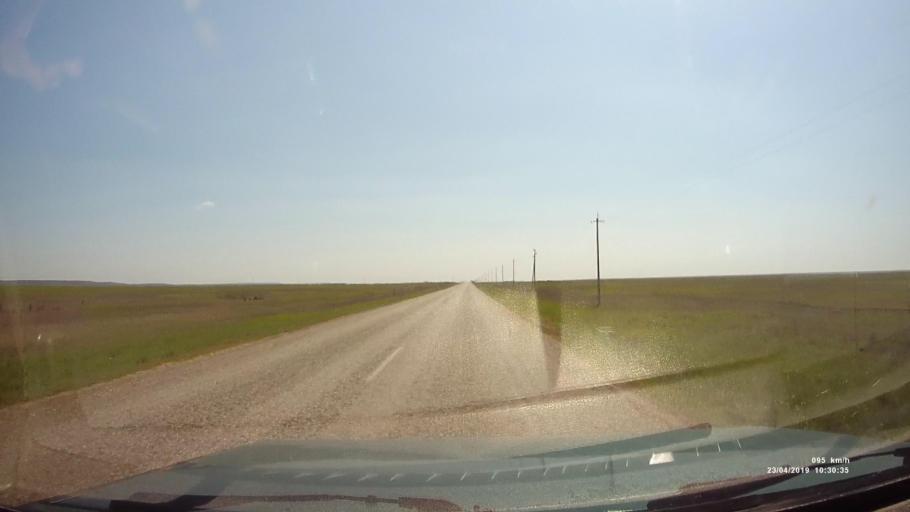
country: RU
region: Kalmykiya
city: Yashalta
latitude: 46.5911
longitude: 42.5473
